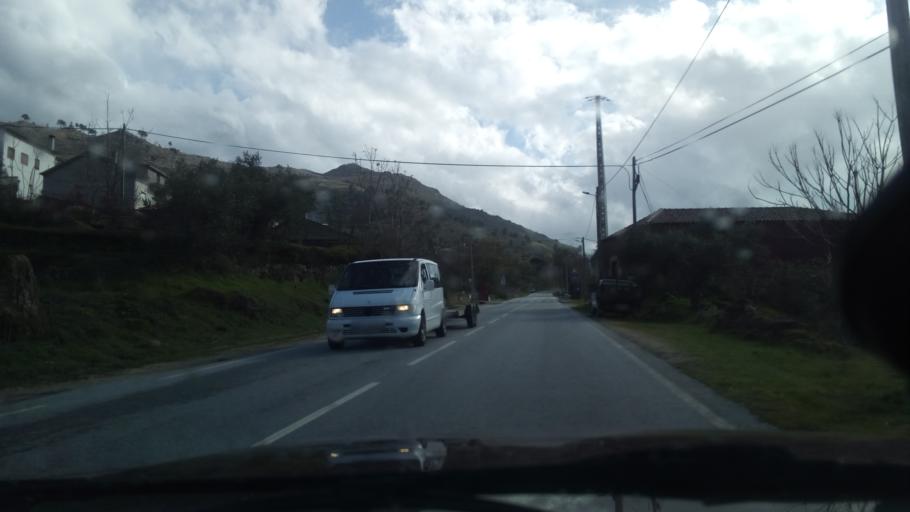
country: PT
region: Guarda
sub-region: Guarda
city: Guarda
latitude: 40.5897
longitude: -7.2902
